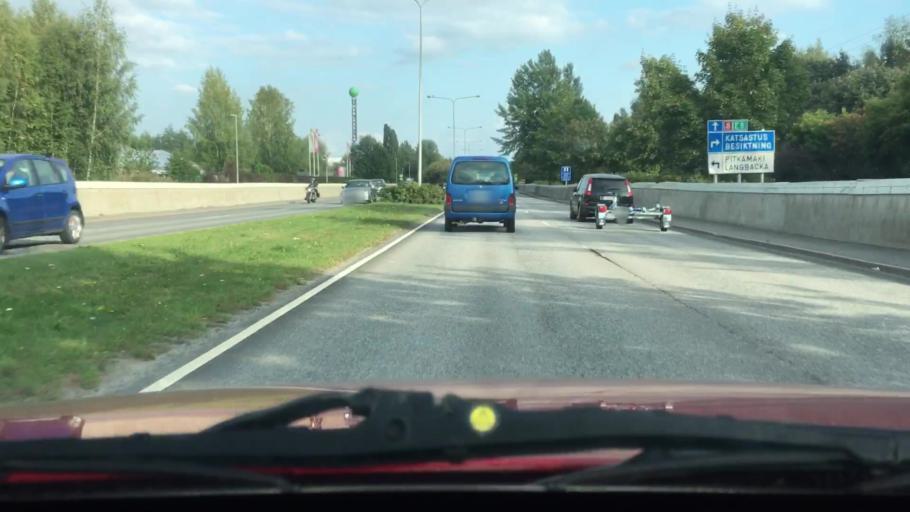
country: FI
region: Varsinais-Suomi
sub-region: Turku
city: Turku
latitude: 60.4582
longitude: 22.2217
